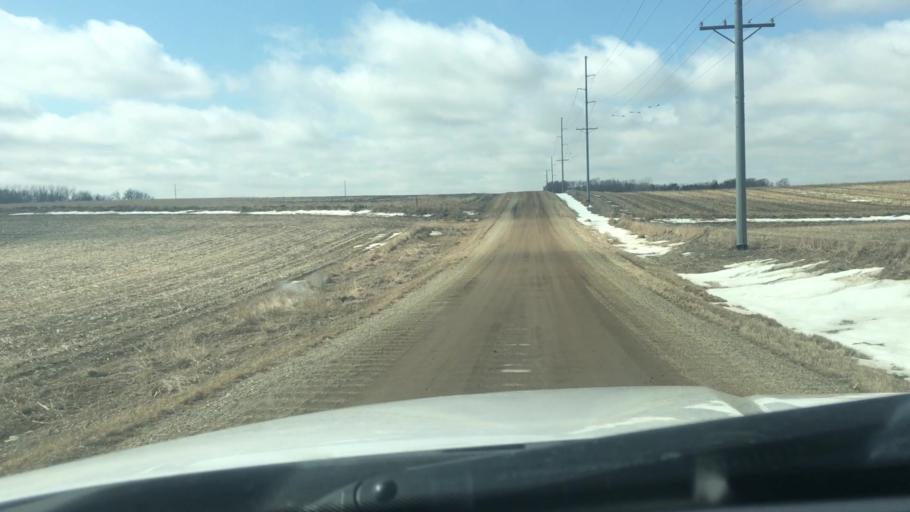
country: US
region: South Dakota
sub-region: Minnehaha County
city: Crooks
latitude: 43.6164
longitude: -96.8047
